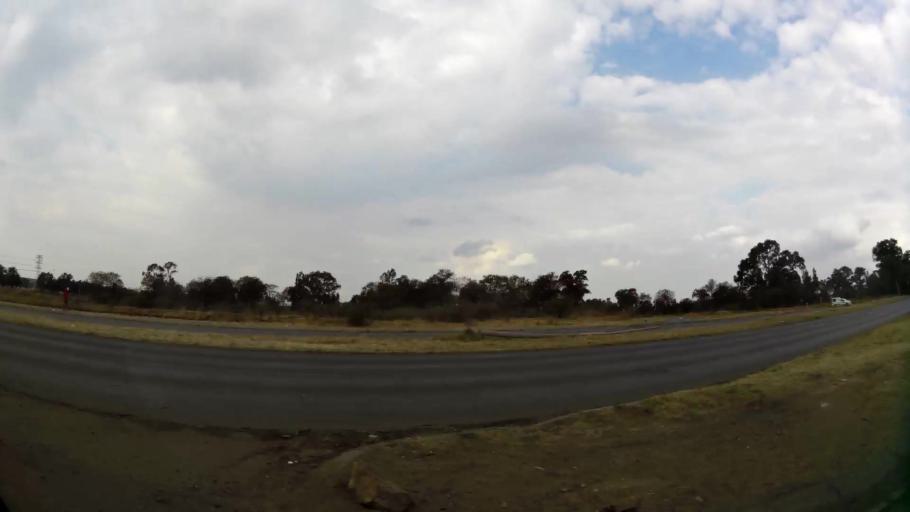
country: ZA
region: Gauteng
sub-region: Sedibeng District Municipality
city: Vanderbijlpark
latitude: -26.6733
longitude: 27.8372
